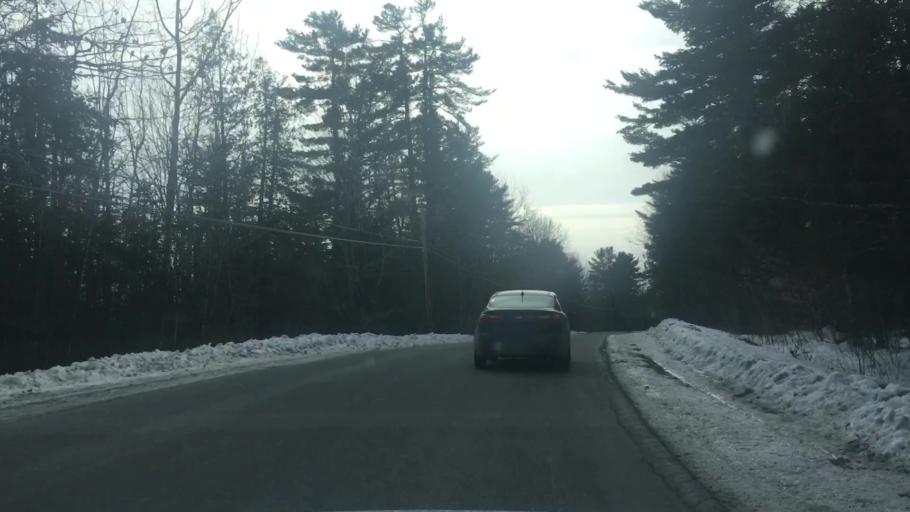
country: US
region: Maine
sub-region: Hancock County
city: Orland
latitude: 44.6273
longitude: -68.6984
